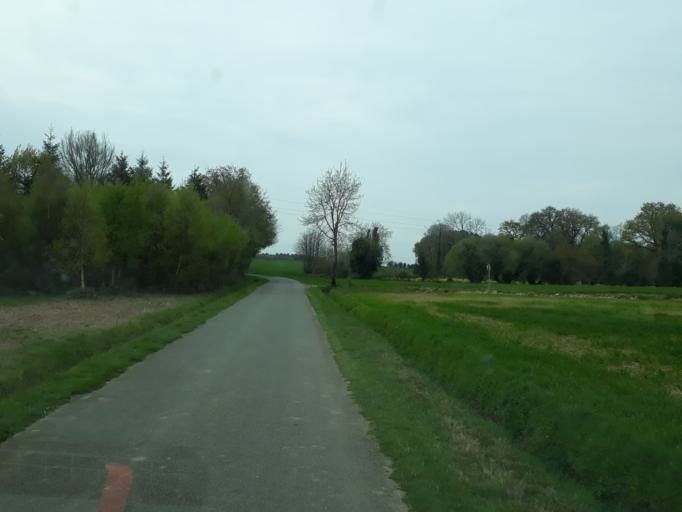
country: FR
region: Brittany
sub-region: Departement du Morbihan
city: Sulniac
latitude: 47.6805
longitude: -2.5882
